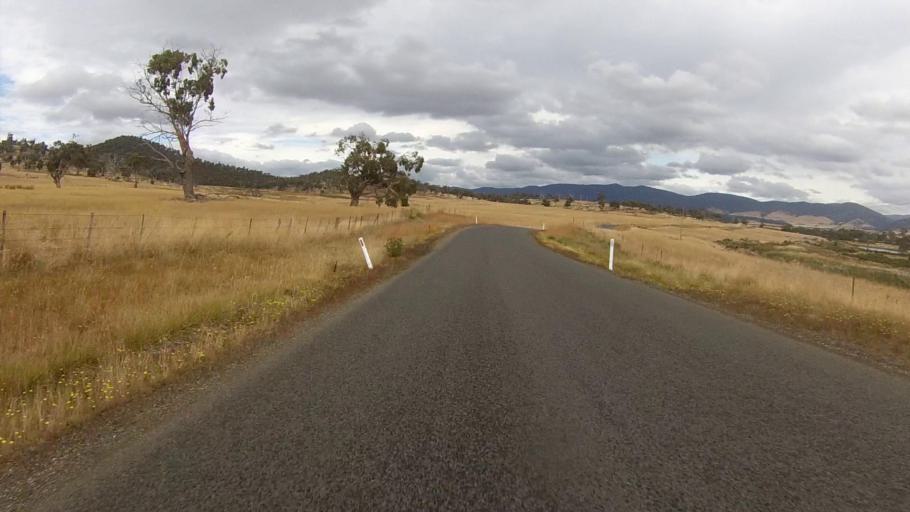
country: AU
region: Tasmania
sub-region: Northern Midlands
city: Evandale
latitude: -41.8017
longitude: 147.7509
